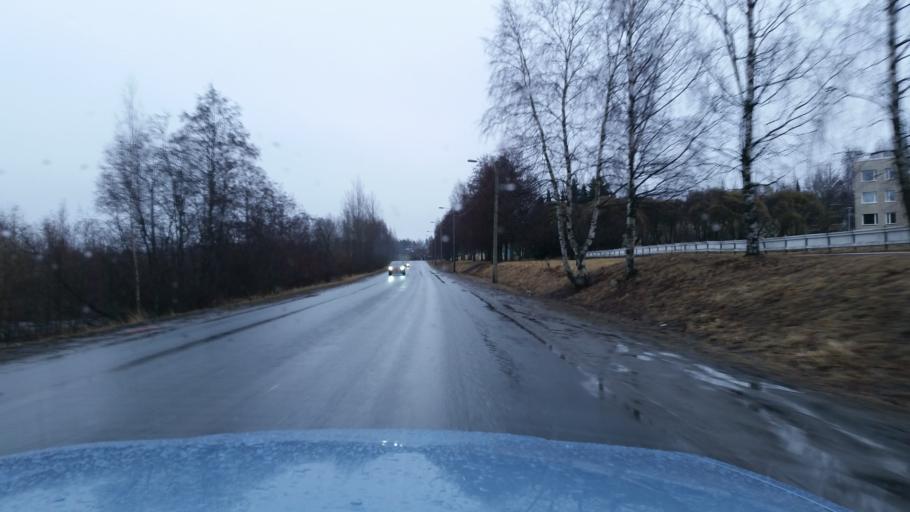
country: FI
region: Pirkanmaa
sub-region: Tampere
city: Tampere
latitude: 61.4823
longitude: 23.8052
